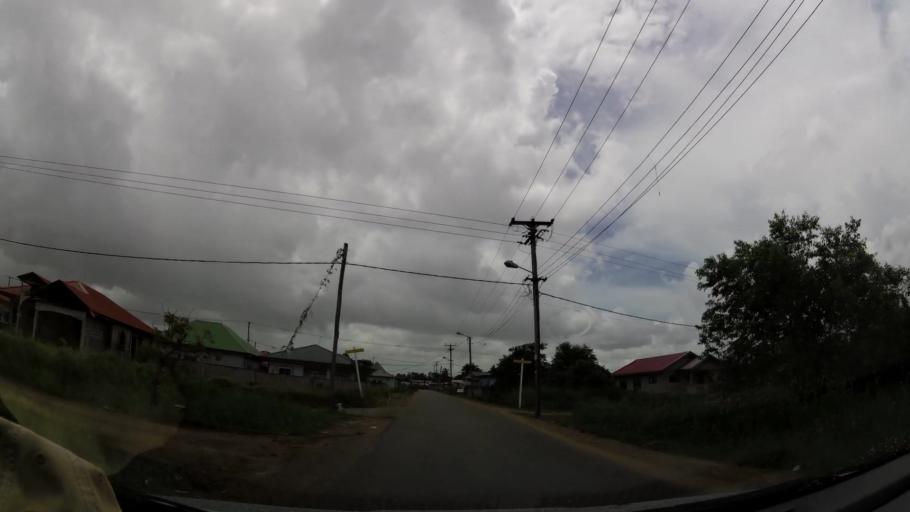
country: SR
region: Wanica
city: Lelydorp
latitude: 5.7888
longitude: -55.2223
